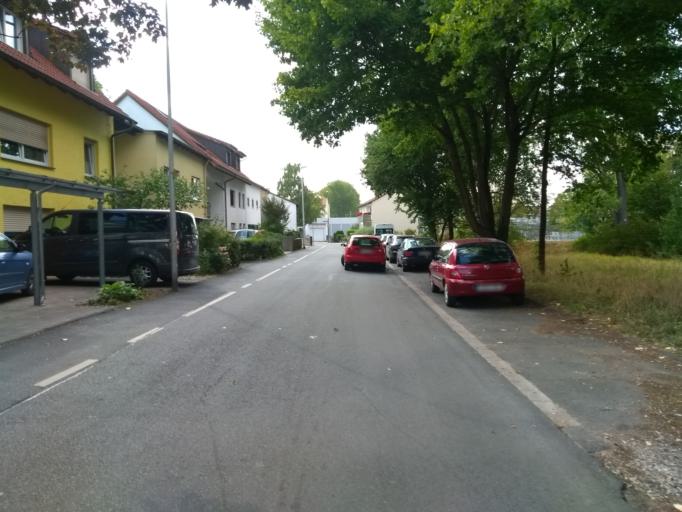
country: DE
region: Bavaria
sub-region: Regierungsbezirk Mittelfranken
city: Erlangen
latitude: 49.5704
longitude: 10.9992
